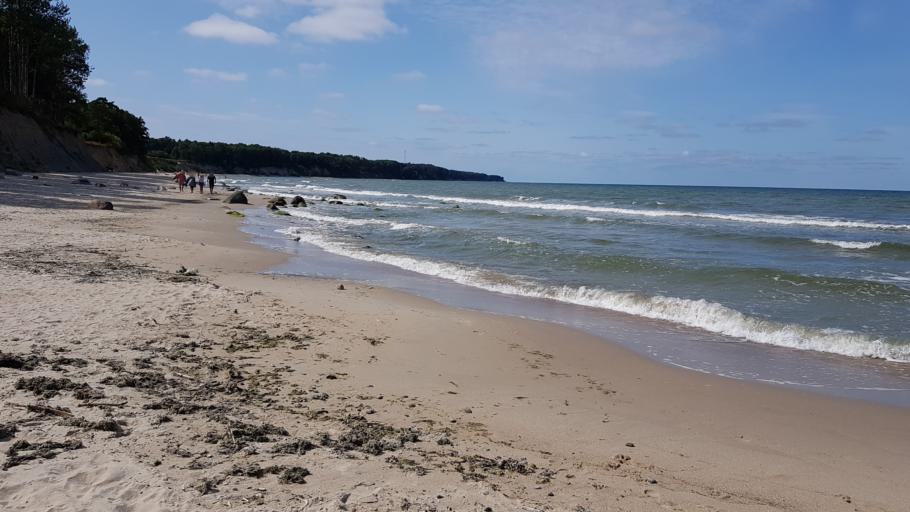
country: RU
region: Kaliningrad
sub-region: Gorod Kaliningrad
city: Pionerskiy
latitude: 54.9414
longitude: 20.3077
